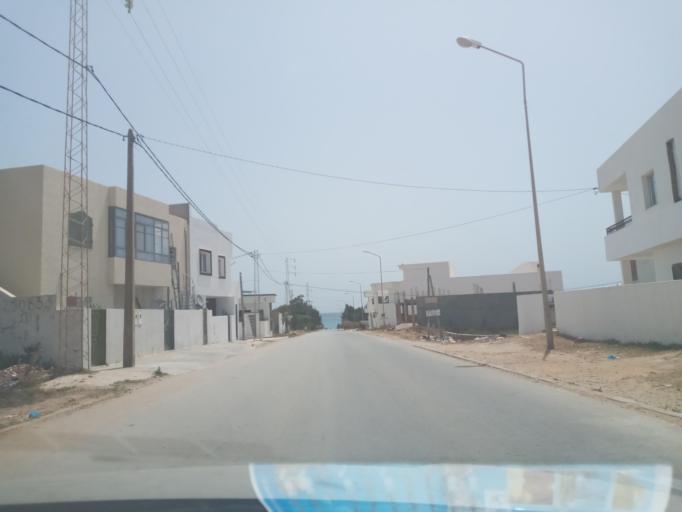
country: TN
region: Nabul
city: El Haouaria
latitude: 37.0365
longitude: 11.0538
